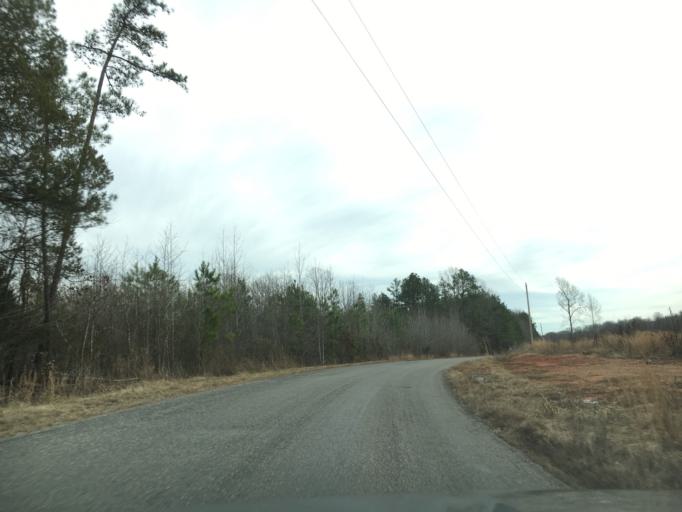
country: US
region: Virginia
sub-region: Amelia County
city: Amelia Court House
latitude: 37.4235
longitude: -77.9939
